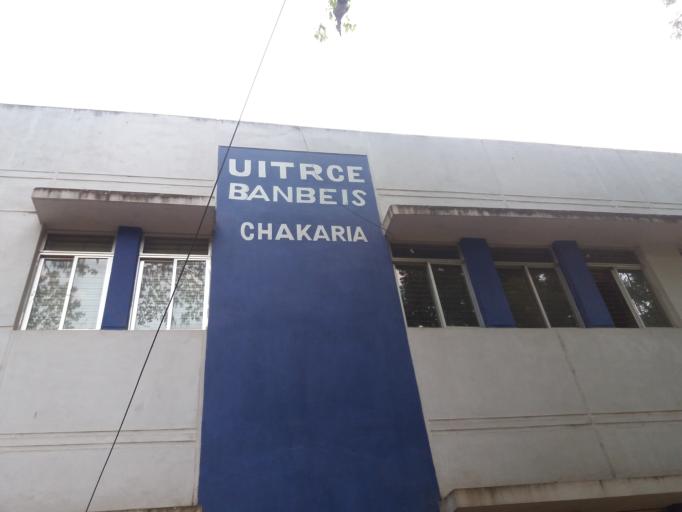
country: BD
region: Chittagong
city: Cox's Bazar
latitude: 21.7516
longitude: 92.0695
